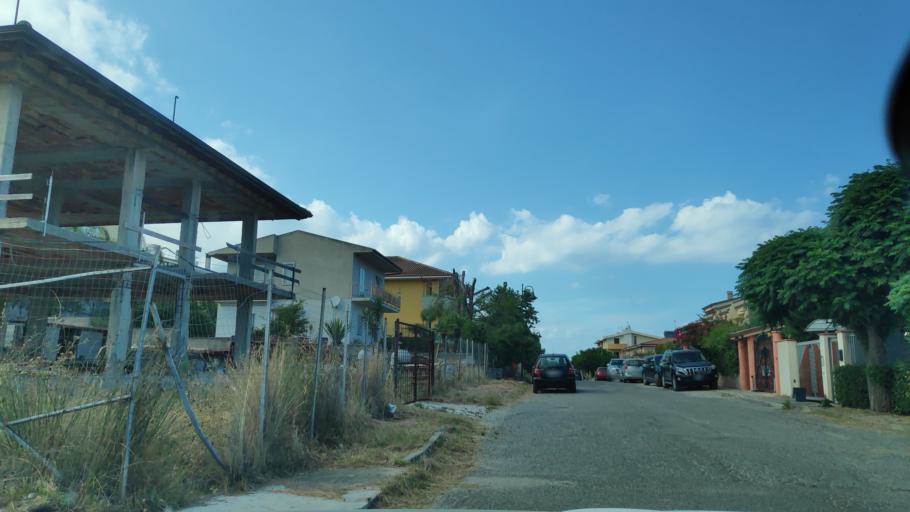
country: IT
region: Calabria
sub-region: Provincia di Catanzaro
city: Guardavalle Marina
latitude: 38.4705
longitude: 16.5779
